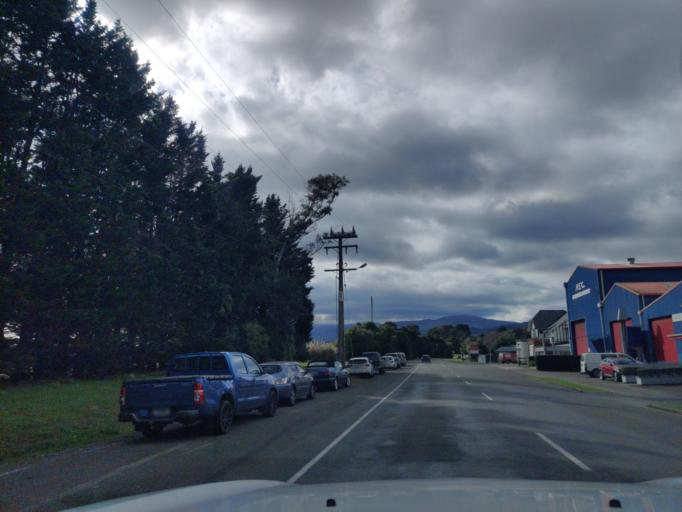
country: NZ
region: Manawatu-Wanganui
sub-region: Palmerston North City
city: Palmerston North
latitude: -40.2980
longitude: 175.7494
